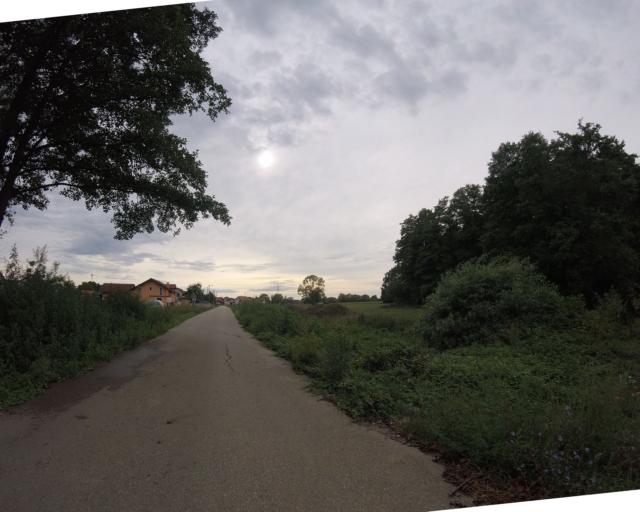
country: HR
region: Zagrebacka
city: Kuce
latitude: 45.7110
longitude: 16.1662
